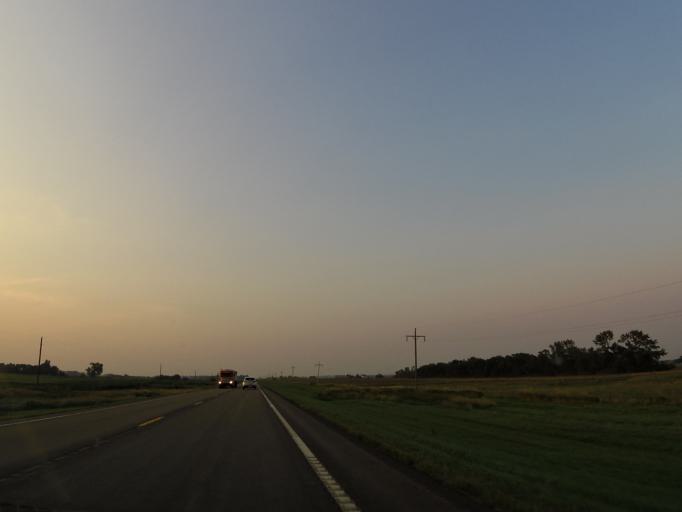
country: US
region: North Dakota
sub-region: Grand Forks County
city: Larimore
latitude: 48.1135
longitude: -97.6223
